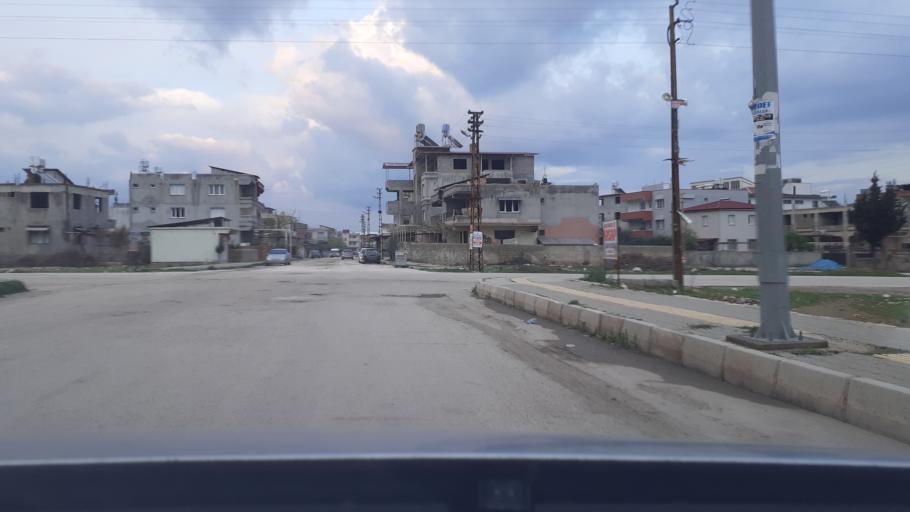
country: TR
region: Hatay
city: Kirikhan
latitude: 36.4833
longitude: 36.3551
